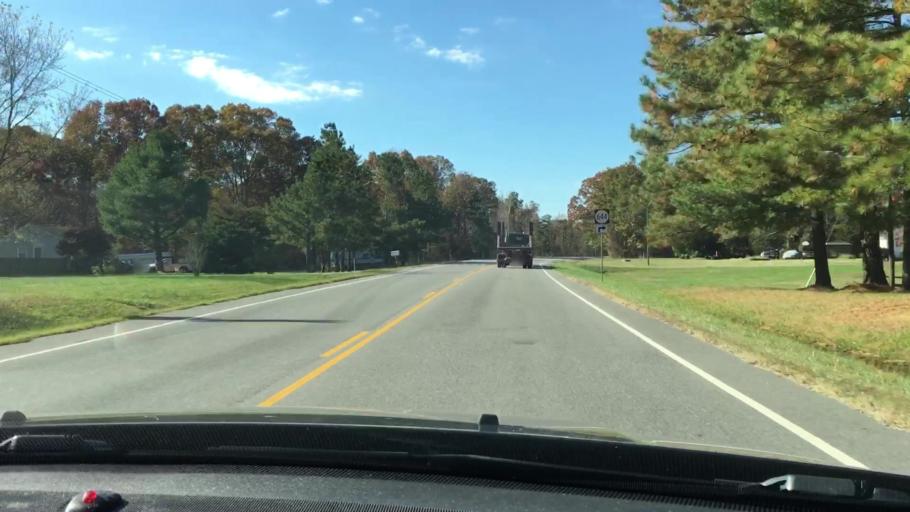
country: US
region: Virginia
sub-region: King William County
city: Central Garage
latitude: 37.7948
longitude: -77.2448
